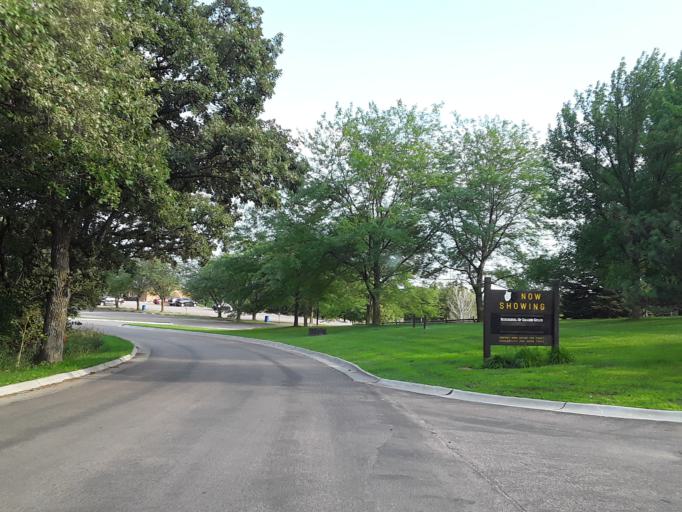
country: US
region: Nebraska
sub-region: Saunders County
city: Ashland
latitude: 41.0286
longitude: -96.3120
